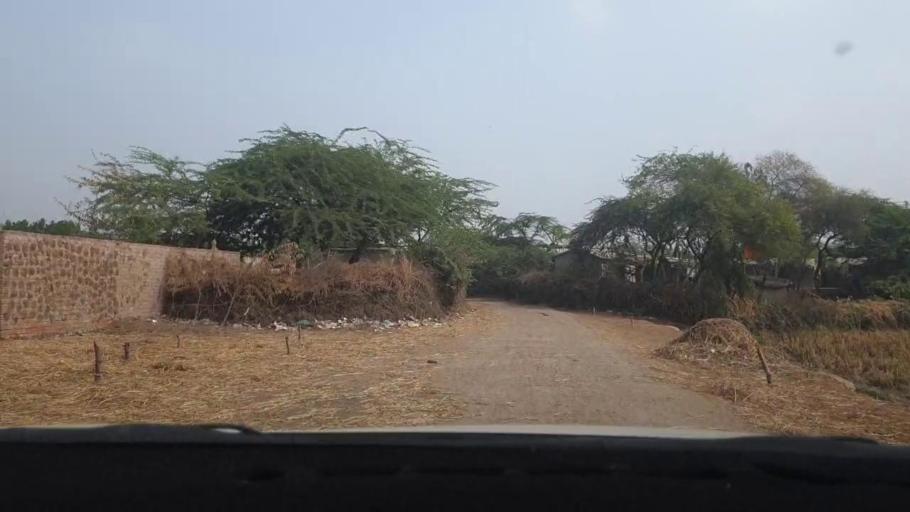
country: PK
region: Sindh
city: Tando Muhammad Khan
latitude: 25.0588
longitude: 68.5374
